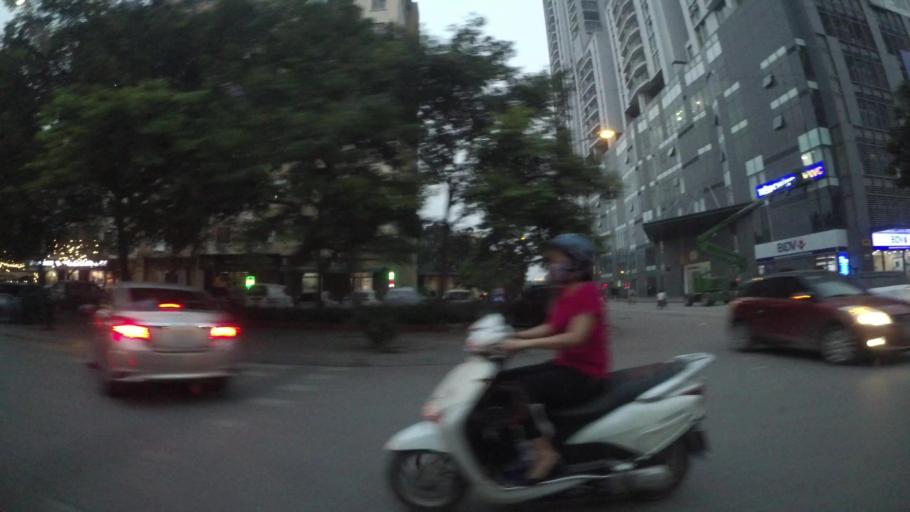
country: VN
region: Ha Noi
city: Ha Dong
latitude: 20.9765
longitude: 105.7888
